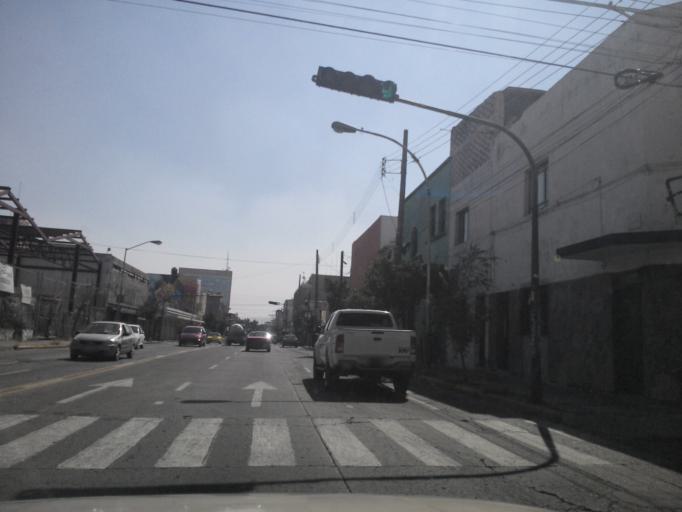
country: MX
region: Jalisco
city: Guadalajara
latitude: 20.6800
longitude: -103.3593
